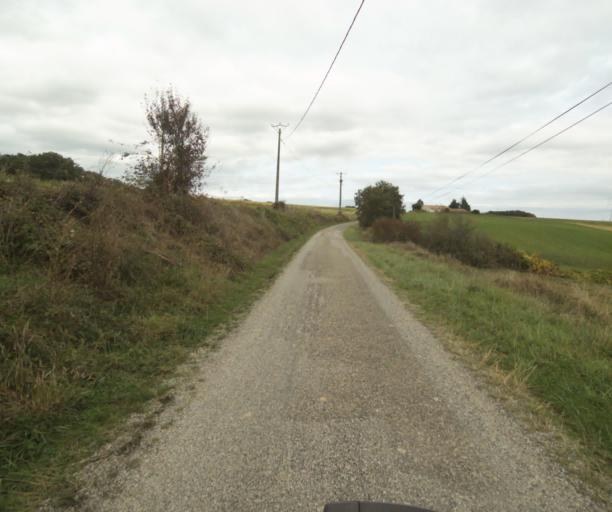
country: FR
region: Midi-Pyrenees
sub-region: Departement du Tarn-et-Garonne
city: Beaumont-de-Lomagne
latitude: 43.8533
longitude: 1.1053
